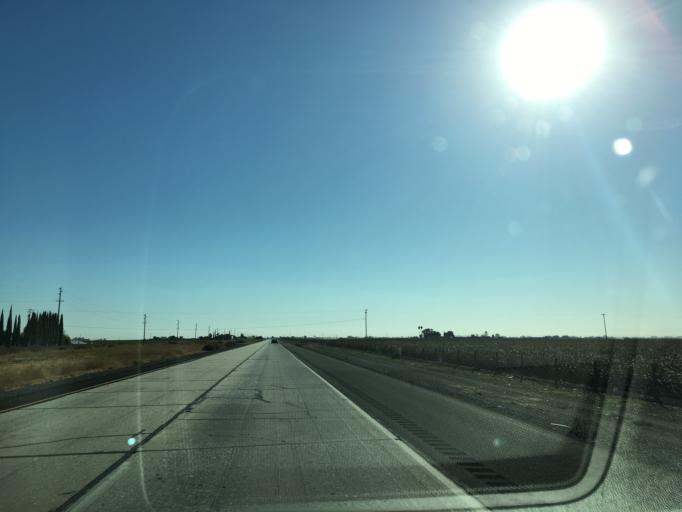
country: US
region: California
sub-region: Merced County
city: South Dos Palos
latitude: 37.0546
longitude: -120.7288
